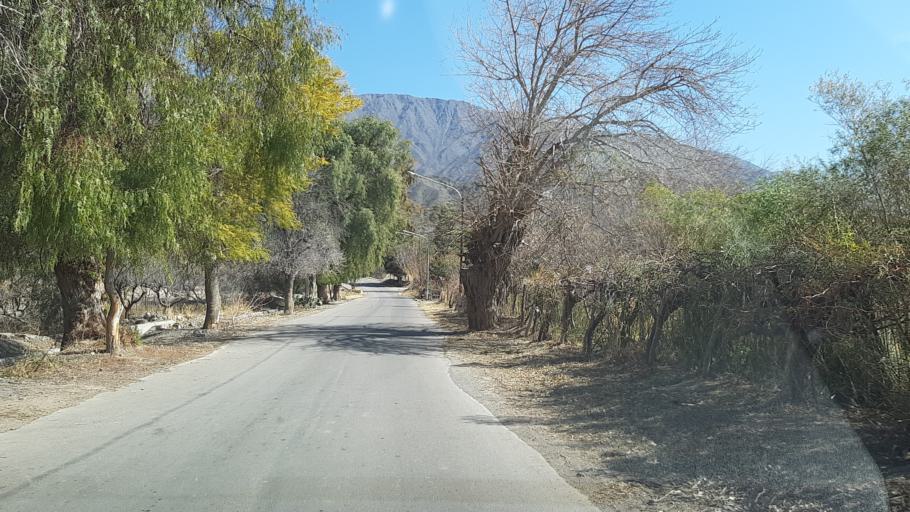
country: AR
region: San Juan
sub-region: Departamento de Zonda
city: Zonda
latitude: -31.5715
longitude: -68.7549
